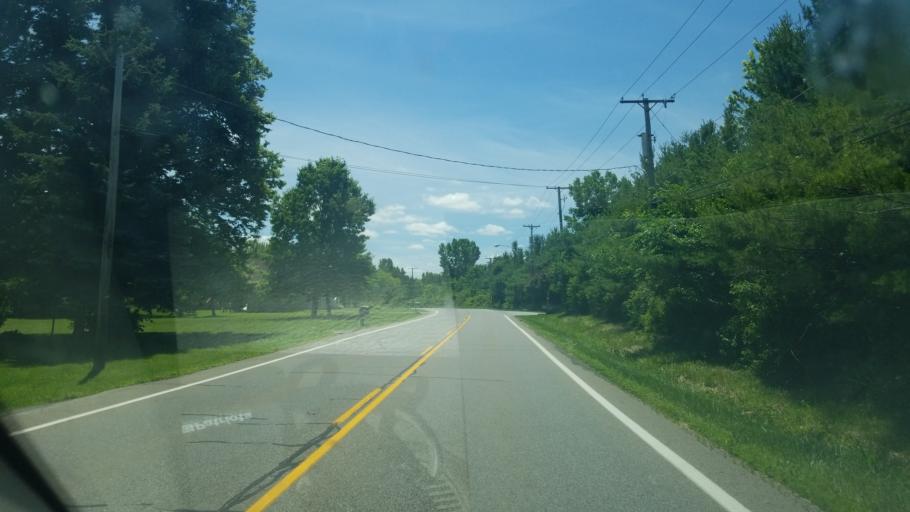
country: US
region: Ohio
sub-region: Columbiana County
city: Columbiana
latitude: 40.9249
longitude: -80.6542
